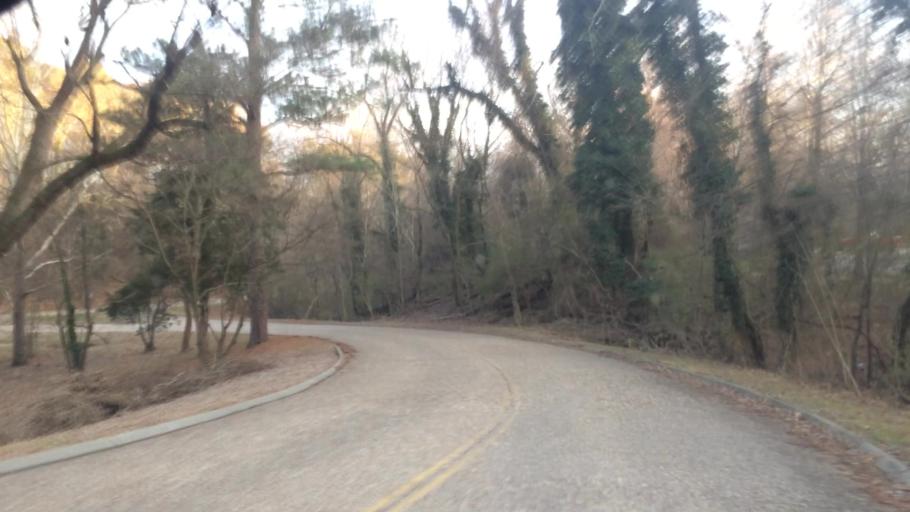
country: US
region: Virginia
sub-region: City of Williamsburg
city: Williamsburg
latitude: 37.2665
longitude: -76.7034
